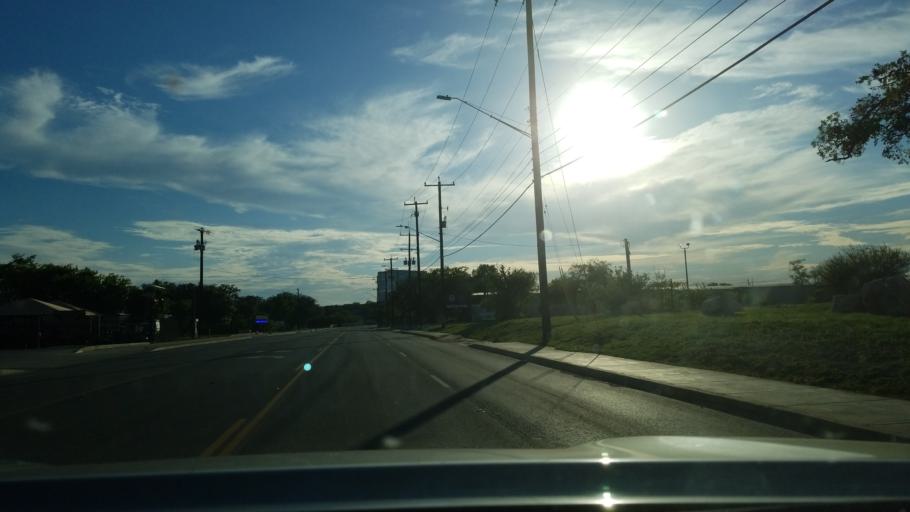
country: US
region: Texas
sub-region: Bexar County
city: Hollywood Park
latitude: 29.6164
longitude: -98.4506
